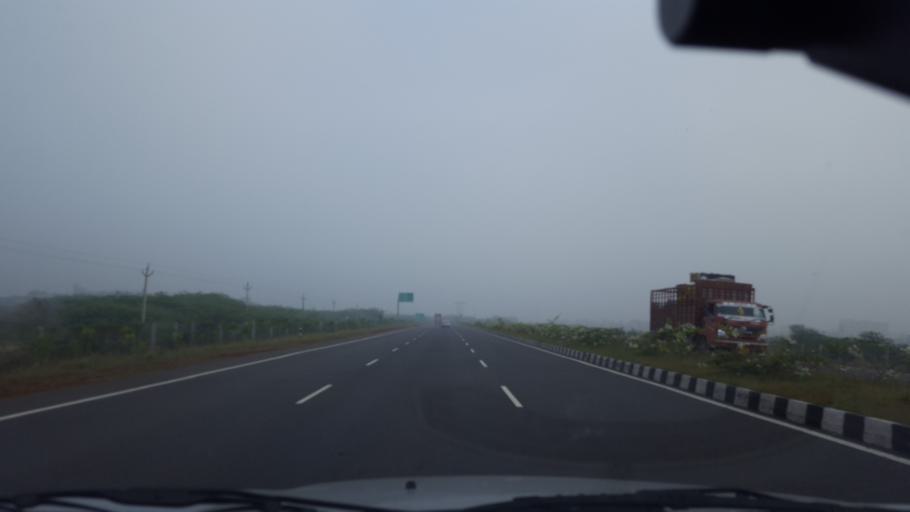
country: IN
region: Andhra Pradesh
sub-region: Prakasam
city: Ongole
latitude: 15.4900
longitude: 80.0654
